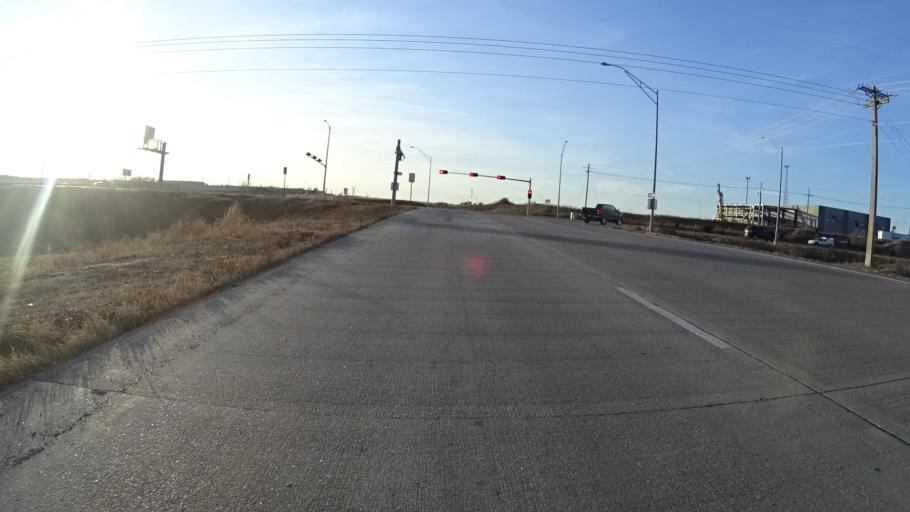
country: US
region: Nebraska
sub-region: Sarpy County
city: Chalco
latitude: 41.1484
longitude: -96.1380
